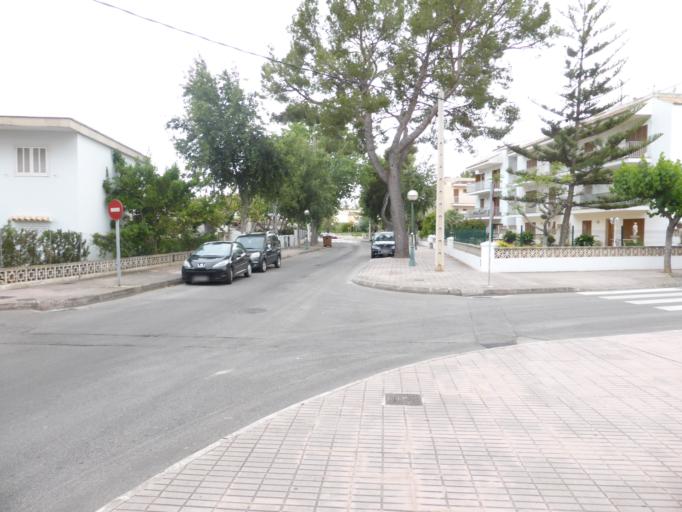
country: ES
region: Balearic Islands
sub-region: Illes Balears
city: Port d'Alcudia
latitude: 39.8393
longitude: 3.1210
